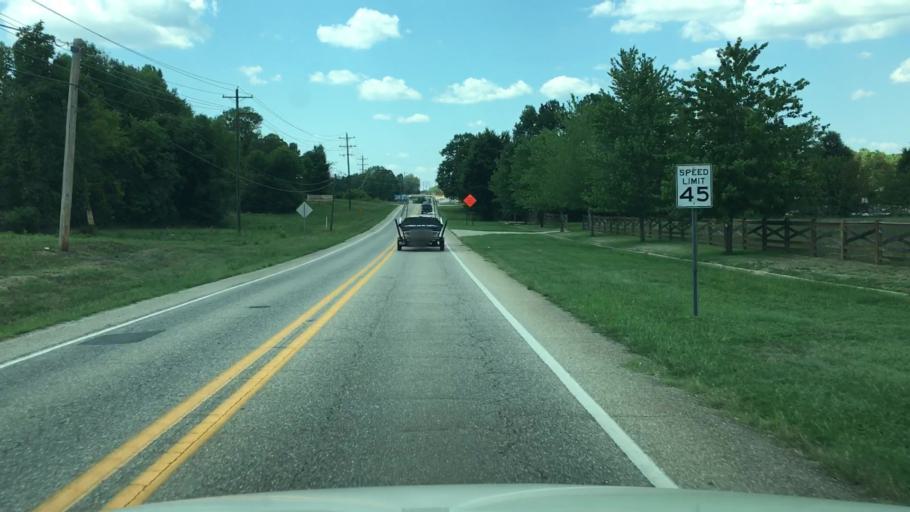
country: US
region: Arkansas
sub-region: Garland County
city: Lake Hamilton
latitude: 34.4086
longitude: -93.0921
